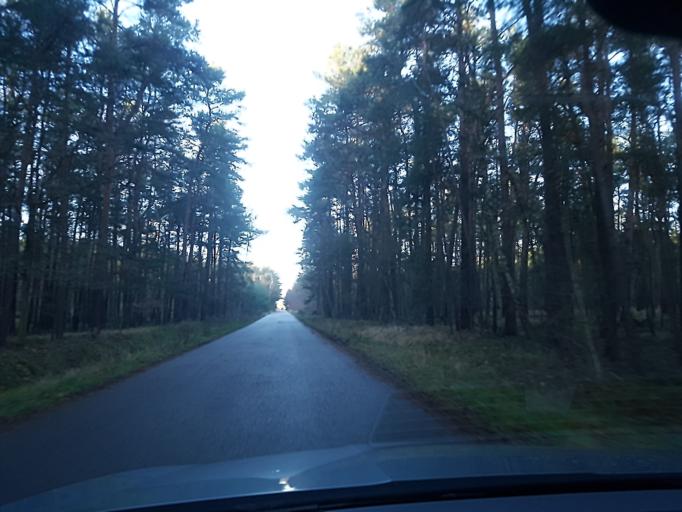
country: DE
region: Brandenburg
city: Schilda
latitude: 51.5973
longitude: 13.3865
